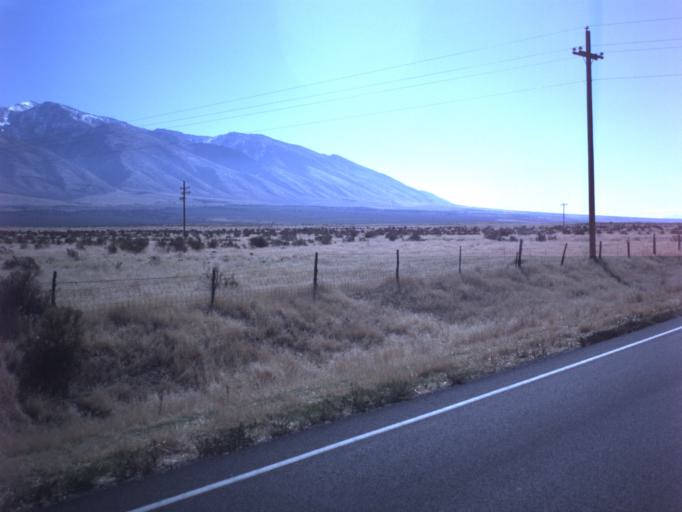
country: US
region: Utah
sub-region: Tooele County
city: Grantsville
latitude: 40.5233
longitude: -112.7477
